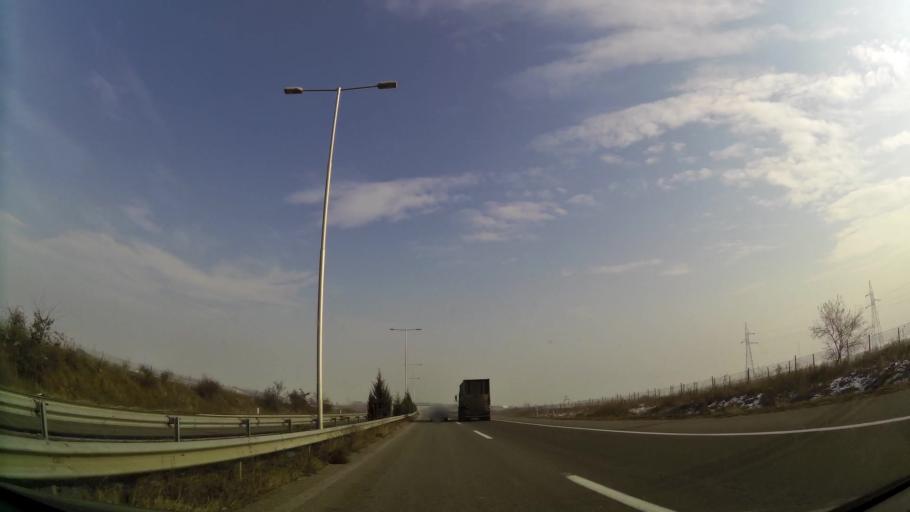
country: MK
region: Butel
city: Butel
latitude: 42.0324
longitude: 21.4805
